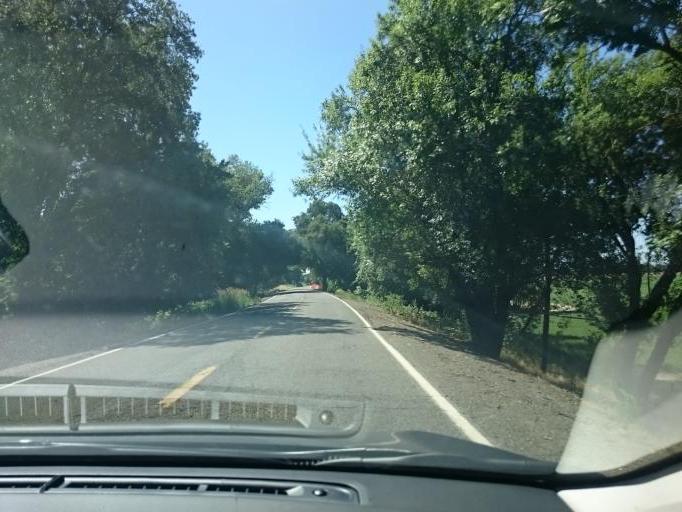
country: US
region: California
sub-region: Yolo County
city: West Sacramento
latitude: 38.4881
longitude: -121.5546
